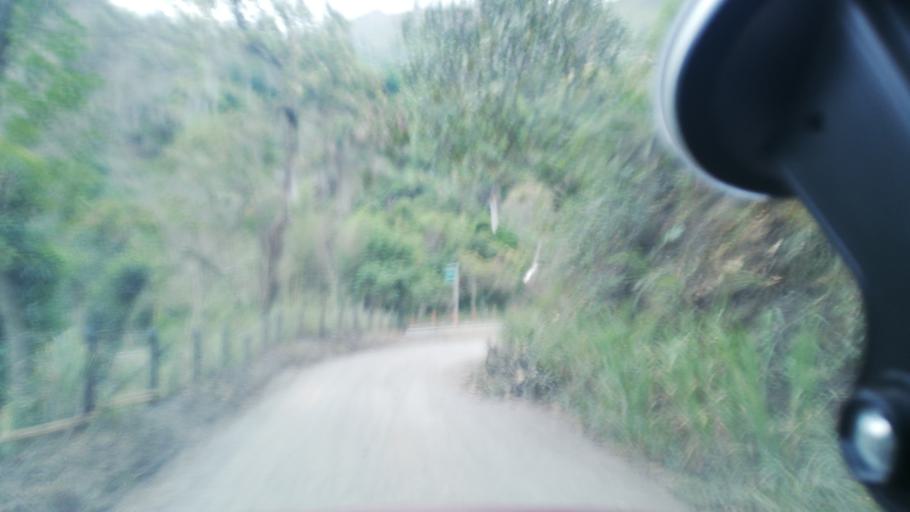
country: CO
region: Cundinamarca
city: Pacho
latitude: 5.1811
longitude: -74.1975
